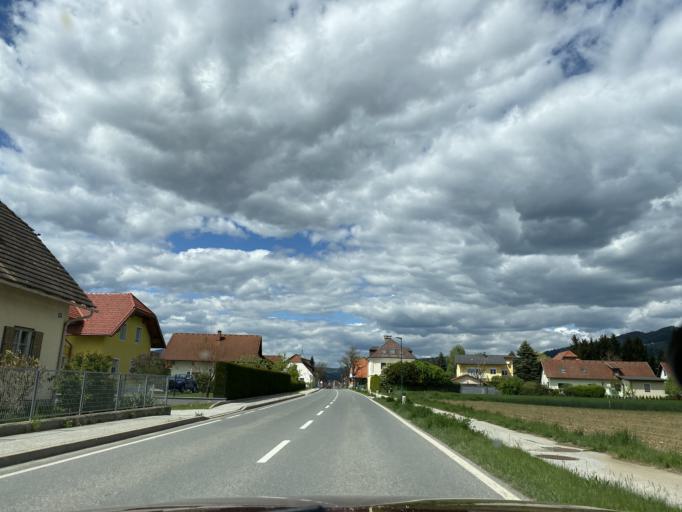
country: AT
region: Carinthia
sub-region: Politischer Bezirk Wolfsberg
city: Wolfsberg
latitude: 46.8017
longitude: 14.8508
